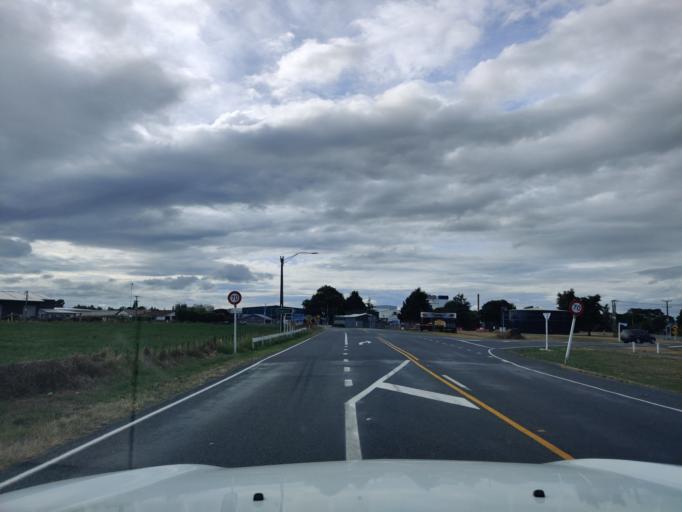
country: NZ
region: Waikato
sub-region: Waipa District
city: Cambridge
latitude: -37.8623
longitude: 175.4551
